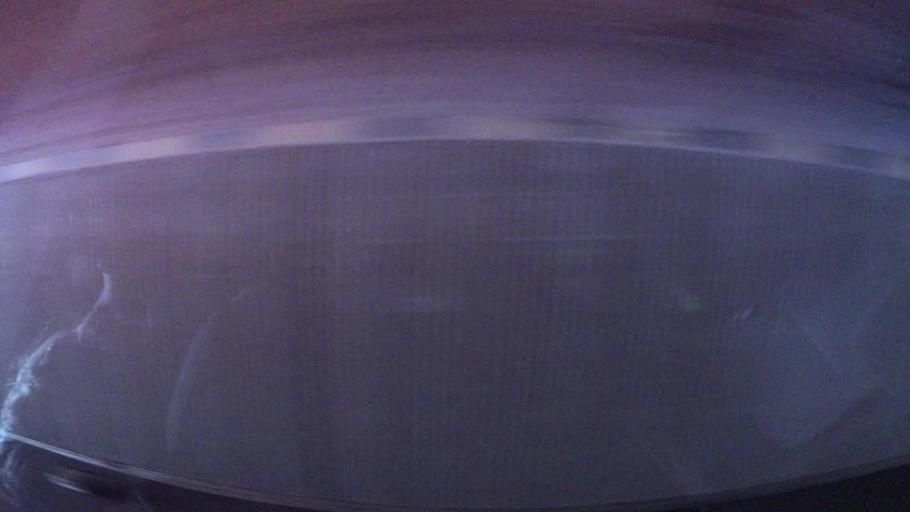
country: JO
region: Zarqa
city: Zarqa
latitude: 32.0611
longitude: 36.0941
